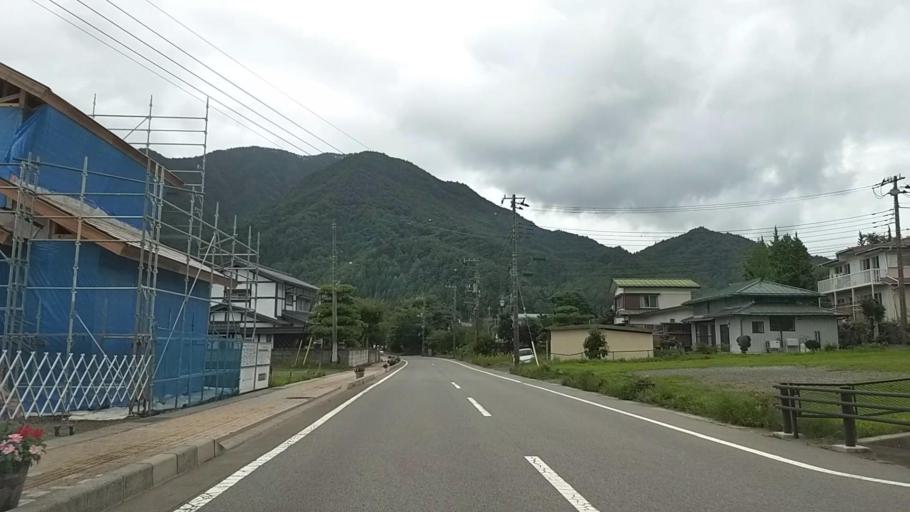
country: JP
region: Yamanashi
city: Fujikawaguchiko
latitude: 35.5096
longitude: 138.7167
